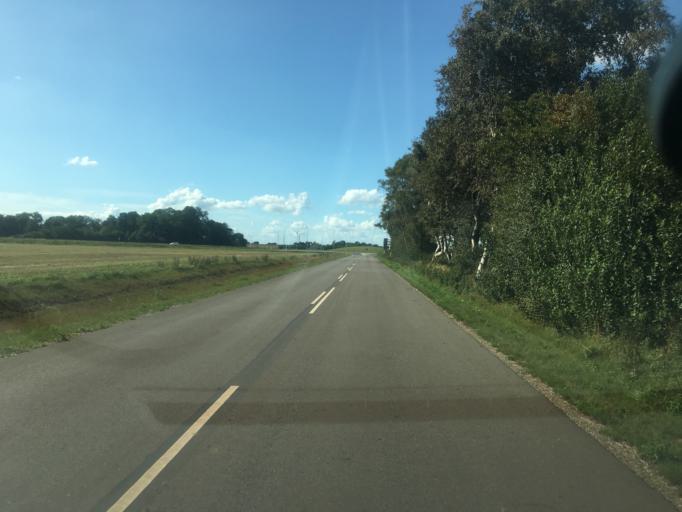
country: DE
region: Schleswig-Holstein
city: Ellhoft
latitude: 54.9685
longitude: 8.9695
